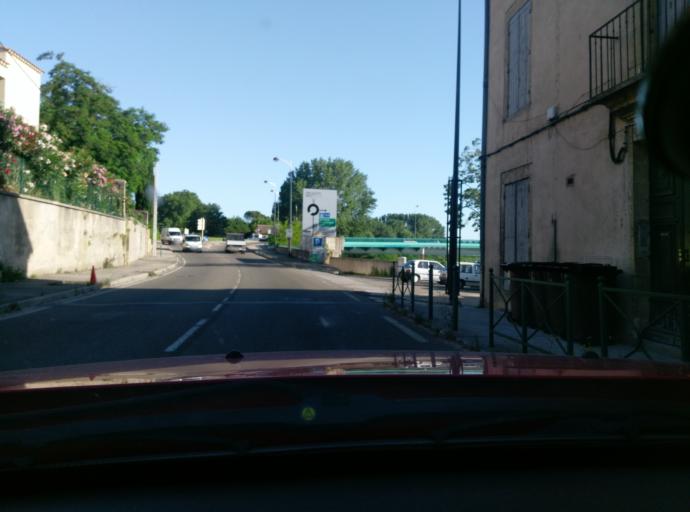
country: FR
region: Languedoc-Roussillon
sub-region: Departement du Gard
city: Remoulins
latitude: 43.9359
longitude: 4.5568
